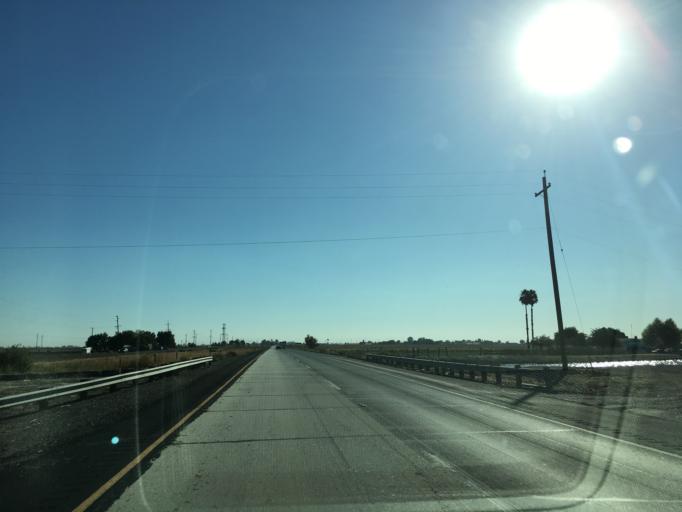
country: US
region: California
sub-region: Merced County
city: Dos Palos
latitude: 37.0541
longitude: -120.6604
